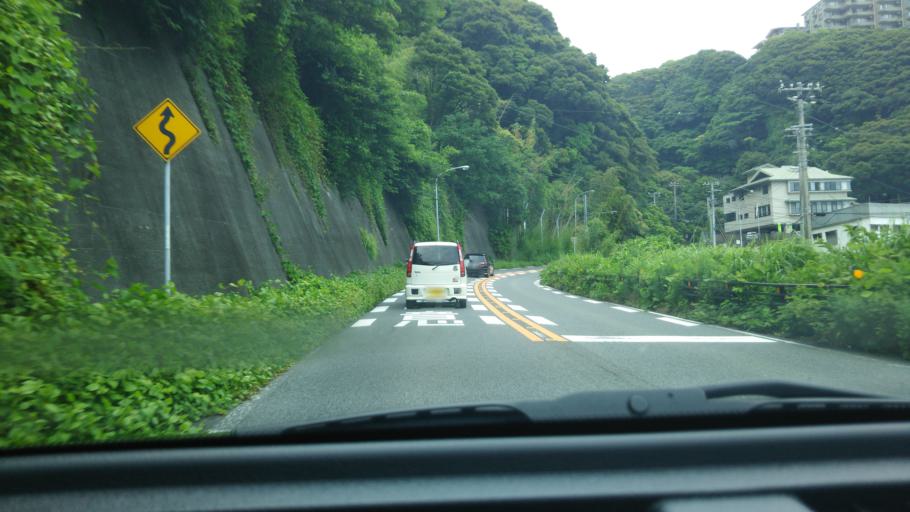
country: JP
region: Shizuoka
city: Ito
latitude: 34.8588
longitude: 139.0861
